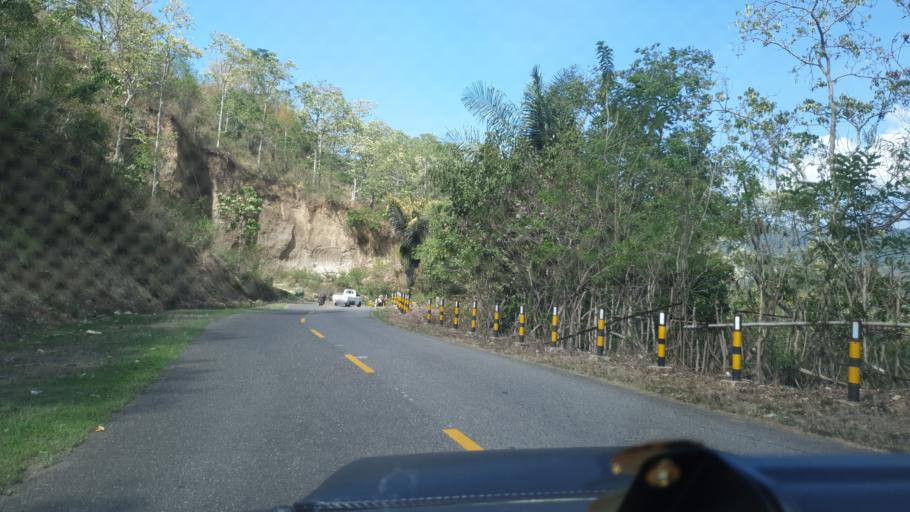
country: ID
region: East Nusa Tenggara
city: Nduaria
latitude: -8.6982
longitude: 121.8130
